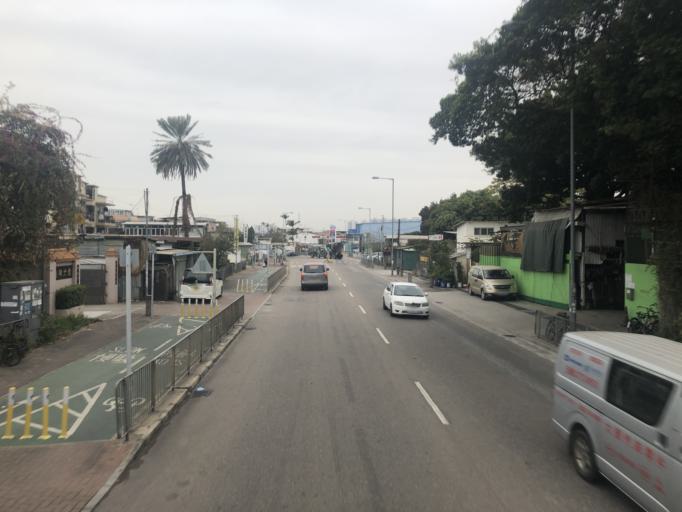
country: HK
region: Yuen Long
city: Yuen Long Kau Hui
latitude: 22.4337
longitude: 113.9926
